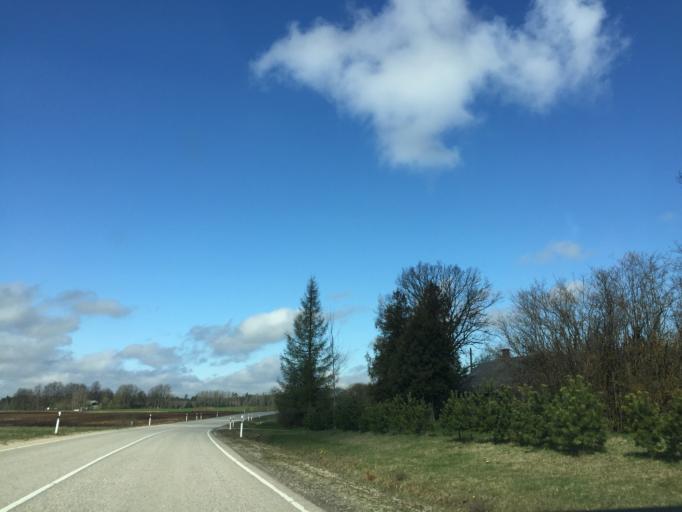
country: LV
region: Apes Novads
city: Ape
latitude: 57.5290
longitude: 26.7326
